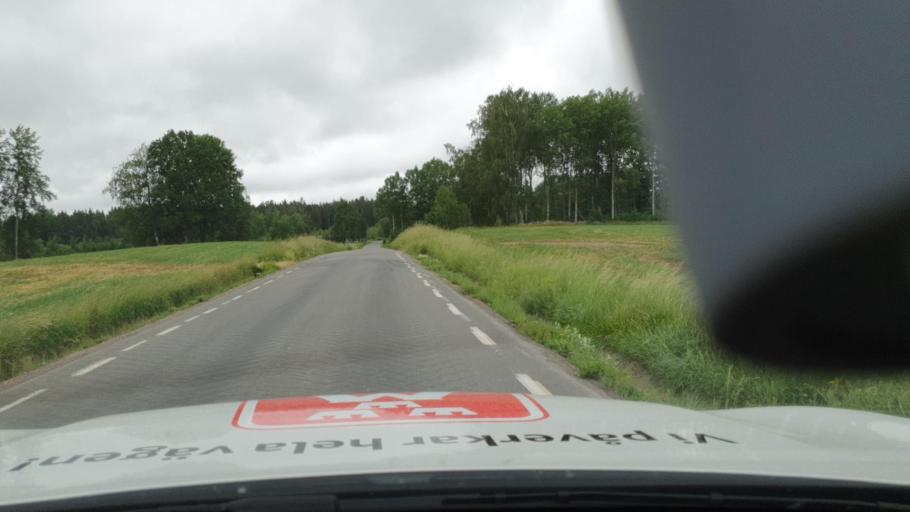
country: SE
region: Vaestra Goetaland
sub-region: Tibro Kommun
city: Tibro
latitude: 58.4074
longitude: 14.0644
